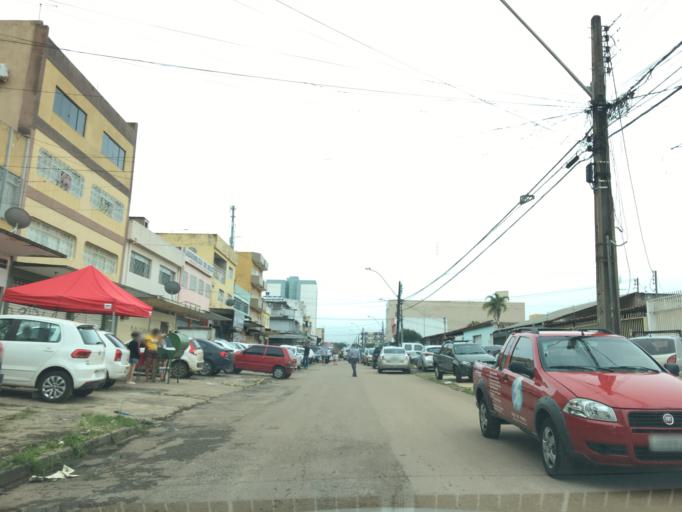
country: BR
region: Federal District
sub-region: Brasilia
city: Brasilia
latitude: -15.8097
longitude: -48.0618
